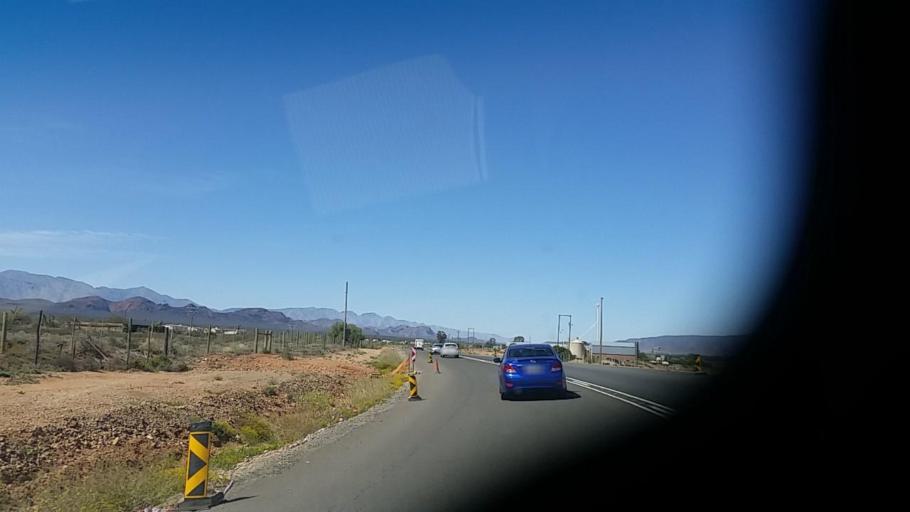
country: ZA
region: Western Cape
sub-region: Eden District Municipality
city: Oudtshoorn
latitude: -33.5858
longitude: 22.2956
